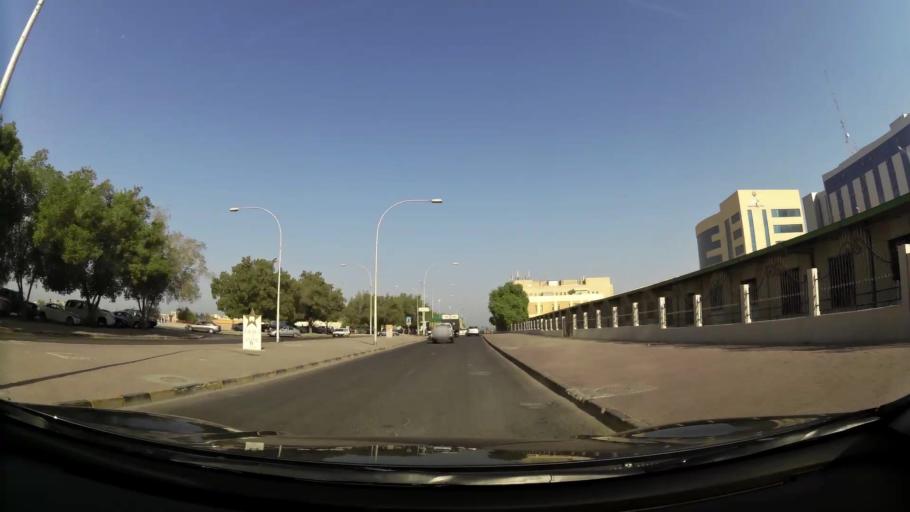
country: KW
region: Al Asimah
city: Kuwait City
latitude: 29.3864
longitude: 47.9869
